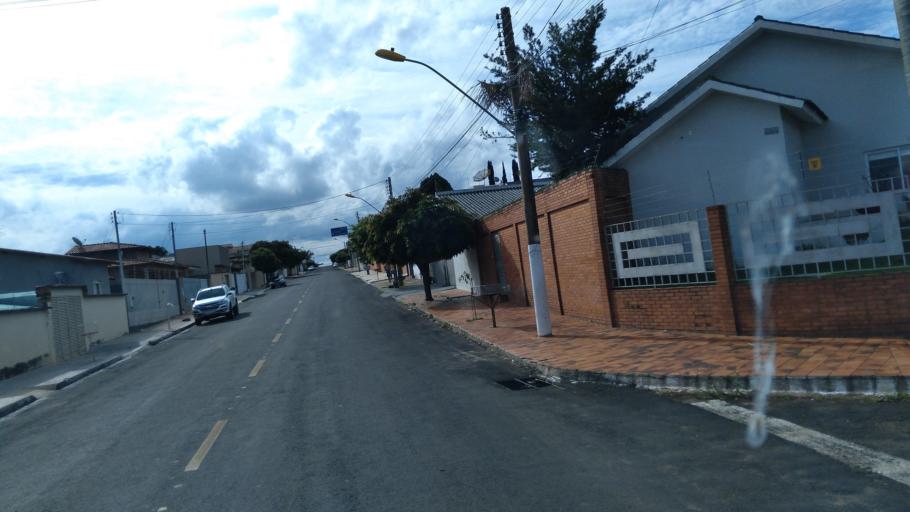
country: BR
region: Goias
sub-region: Mineiros
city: Mineiros
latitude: -17.5639
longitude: -52.5633
